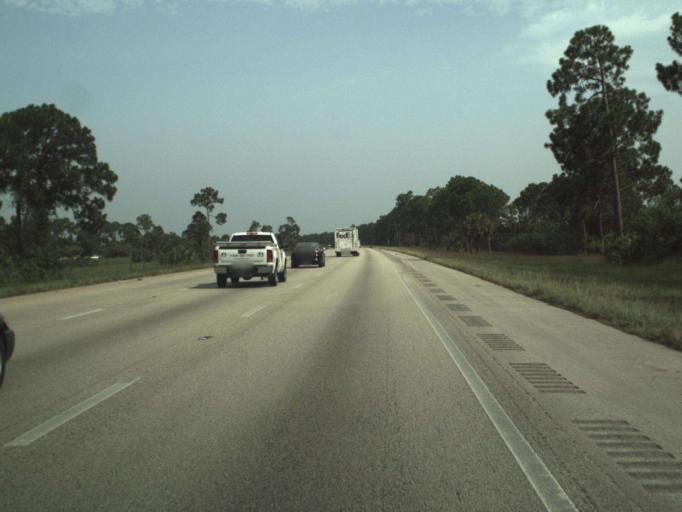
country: US
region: Florida
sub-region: Saint Lucie County
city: Port Saint Lucie
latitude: 27.2439
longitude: -80.4144
